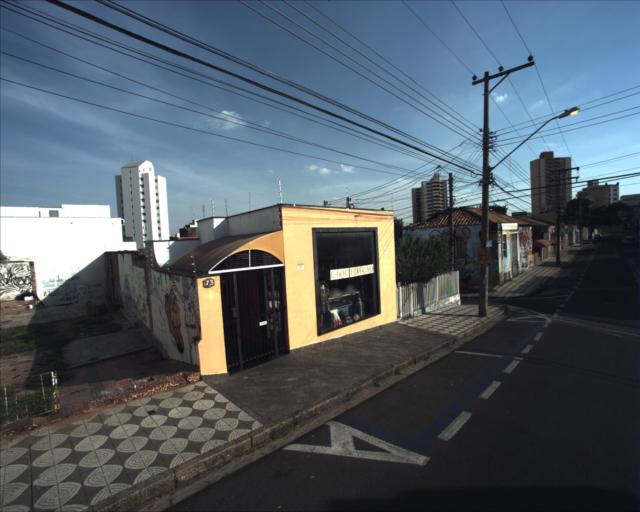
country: BR
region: Sao Paulo
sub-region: Sorocaba
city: Sorocaba
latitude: -23.5039
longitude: -47.4618
